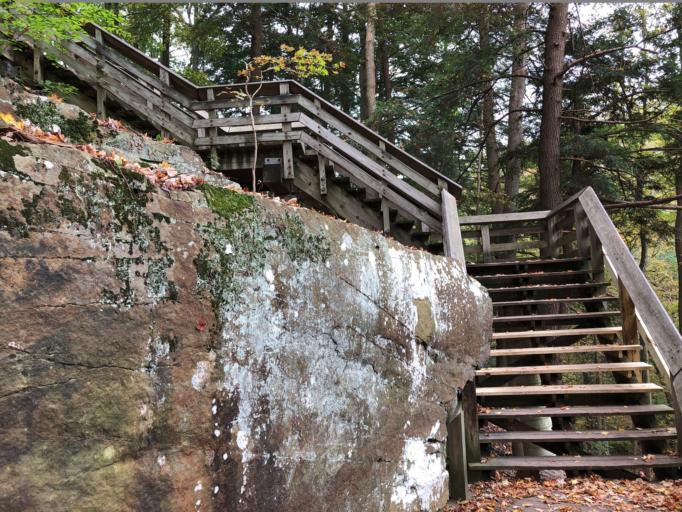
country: US
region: Ohio
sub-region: Summit County
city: Boston Heights
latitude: 41.2771
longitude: -81.5395
